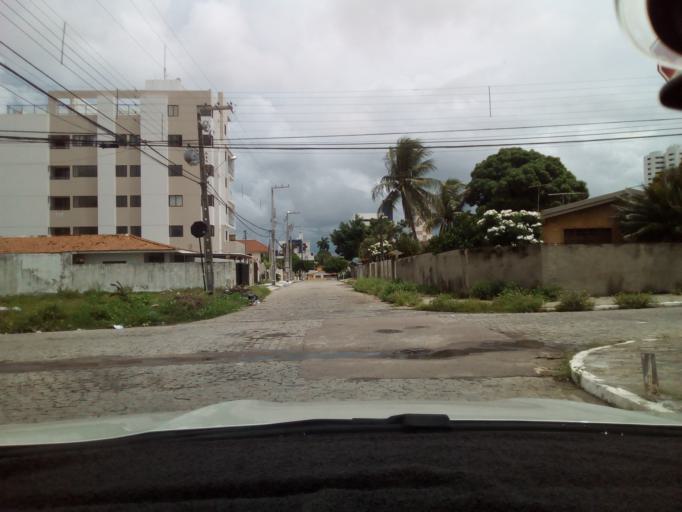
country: BR
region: Paraiba
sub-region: Joao Pessoa
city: Joao Pessoa
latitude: -7.1236
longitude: -34.8487
